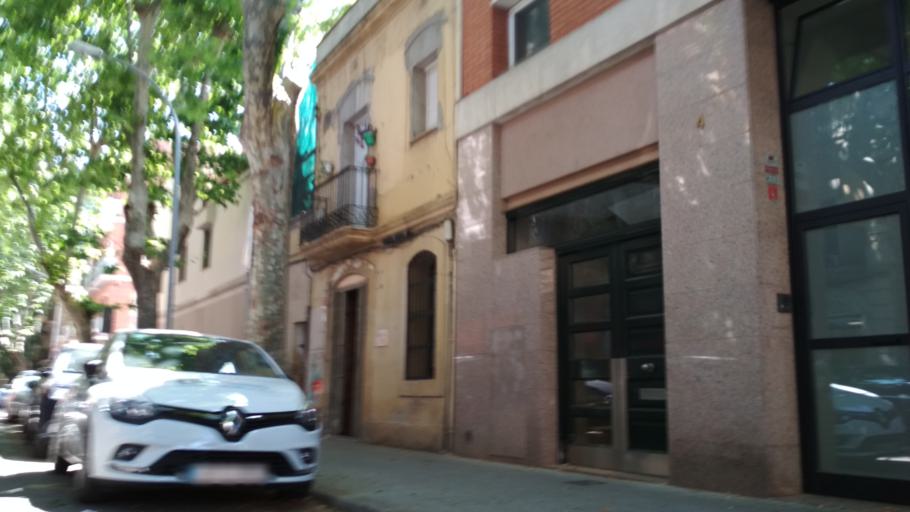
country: ES
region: Catalonia
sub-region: Provincia de Barcelona
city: les Corts
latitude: 41.3775
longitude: 2.1356
